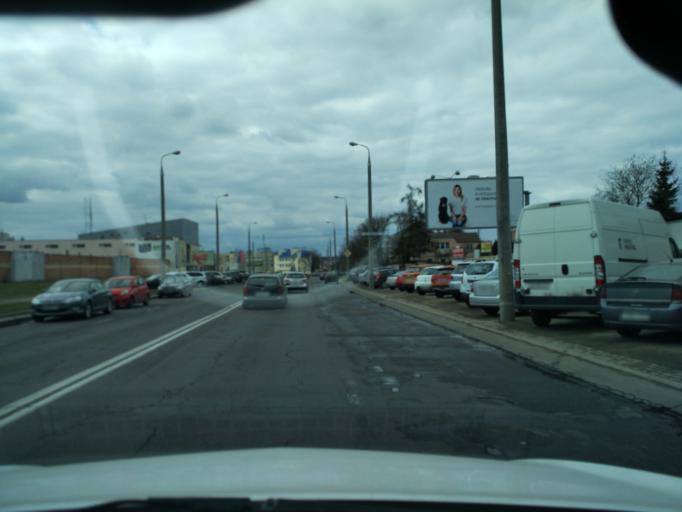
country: BY
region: Minsk
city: Minsk
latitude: 53.9373
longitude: 27.5784
